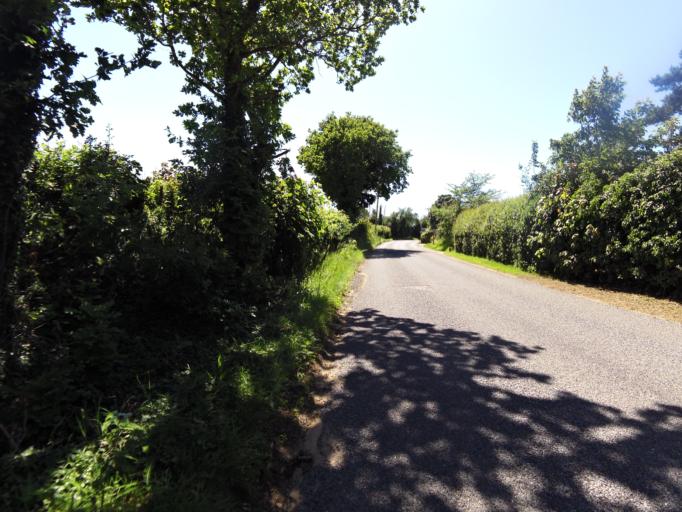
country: GB
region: England
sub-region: Suffolk
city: Felixstowe
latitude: 52.0443
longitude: 1.4258
